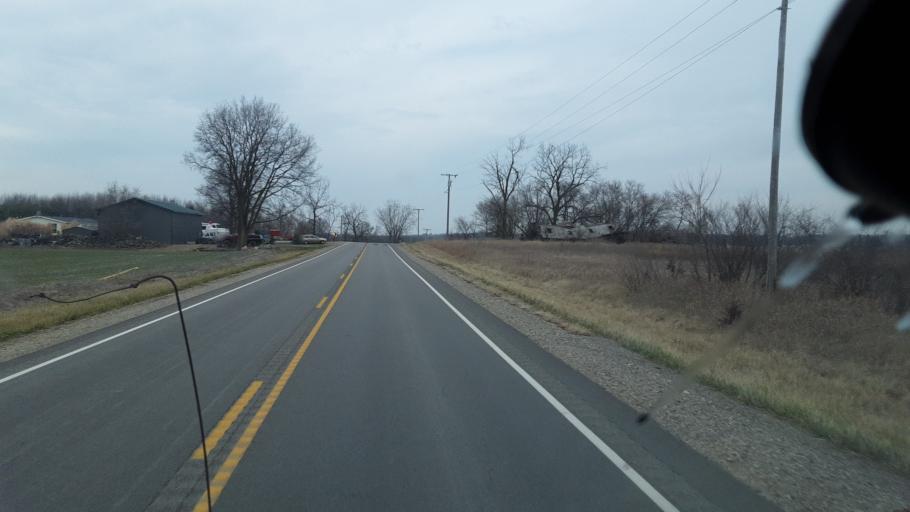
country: US
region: Indiana
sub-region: Noble County
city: Kendallville
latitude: 41.5517
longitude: -85.1709
